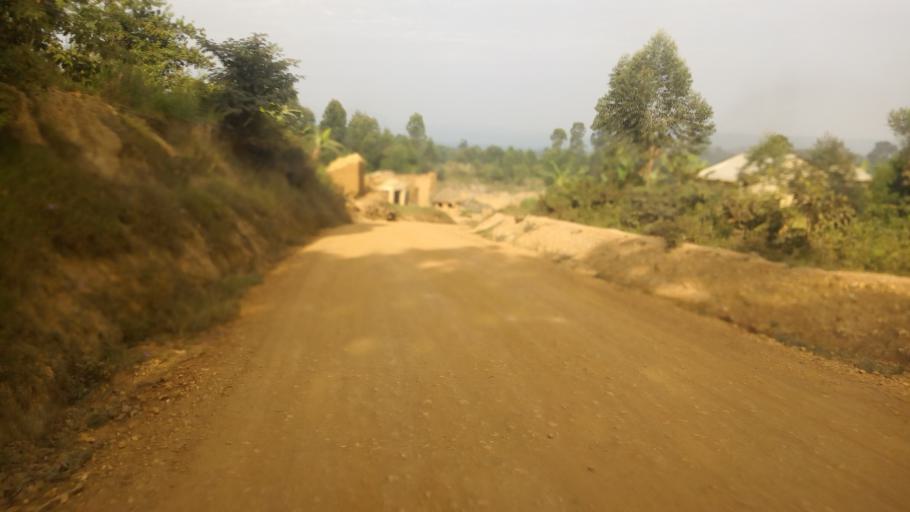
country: UG
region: Western Region
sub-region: Kanungu District
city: Ntungamo
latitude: -0.8347
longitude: 29.6794
